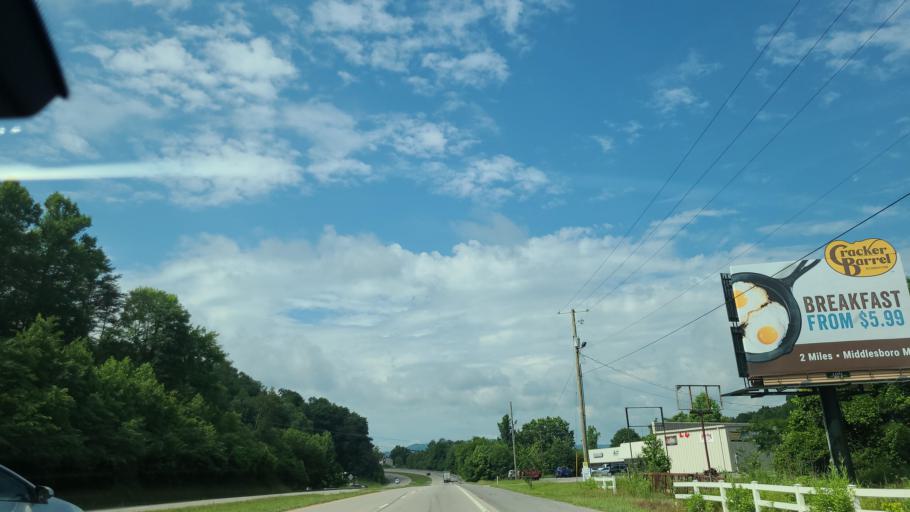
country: US
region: Kentucky
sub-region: Bell County
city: Middlesboro
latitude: 36.6431
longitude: -83.7016
